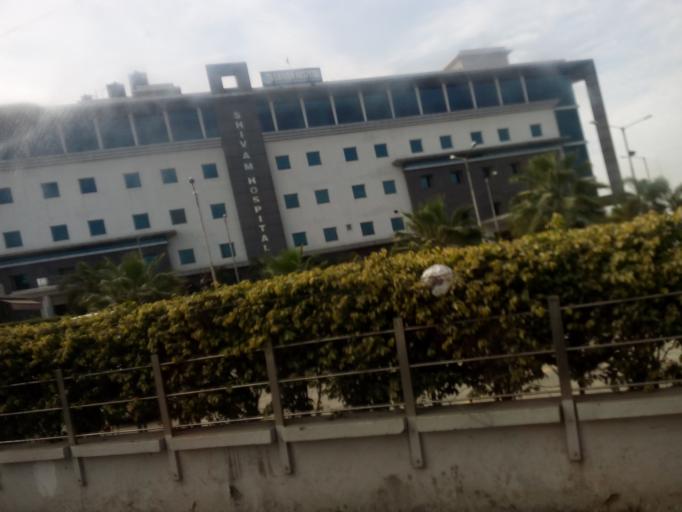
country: IN
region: Punjab
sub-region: Hoshiarpur
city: Hoshiarpur
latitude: 31.5210
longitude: 75.9010
